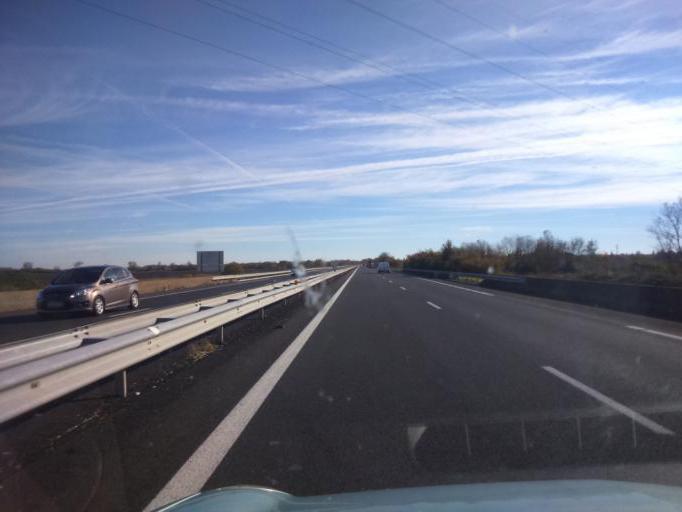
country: FR
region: Poitou-Charentes
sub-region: Departement de la Charente-Maritime
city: Tonnay-Charente
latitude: 45.9574
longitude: -0.9300
